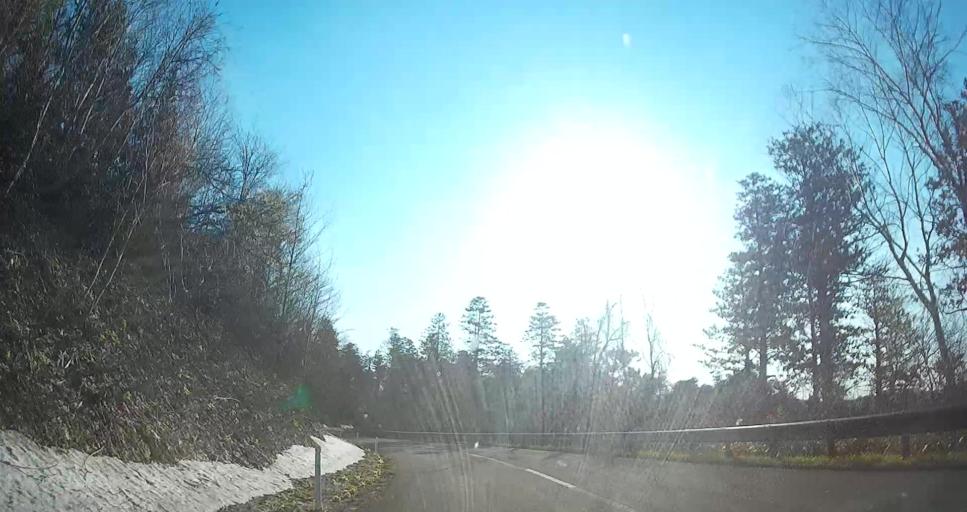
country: JP
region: Aomori
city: Mutsu
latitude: 41.3122
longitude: 141.1112
